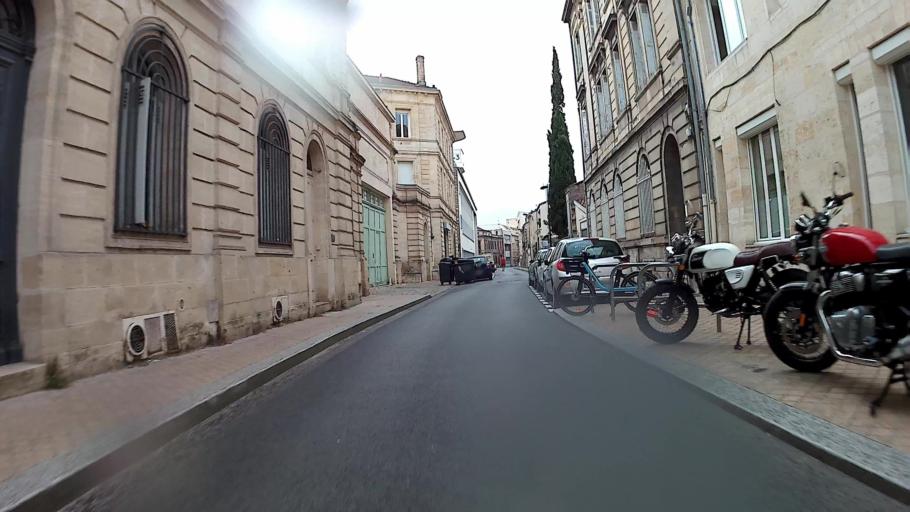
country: FR
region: Aquitaine
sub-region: Departement de la Gironde
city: Le Bouscat
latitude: 44.8518
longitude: -0.5910
